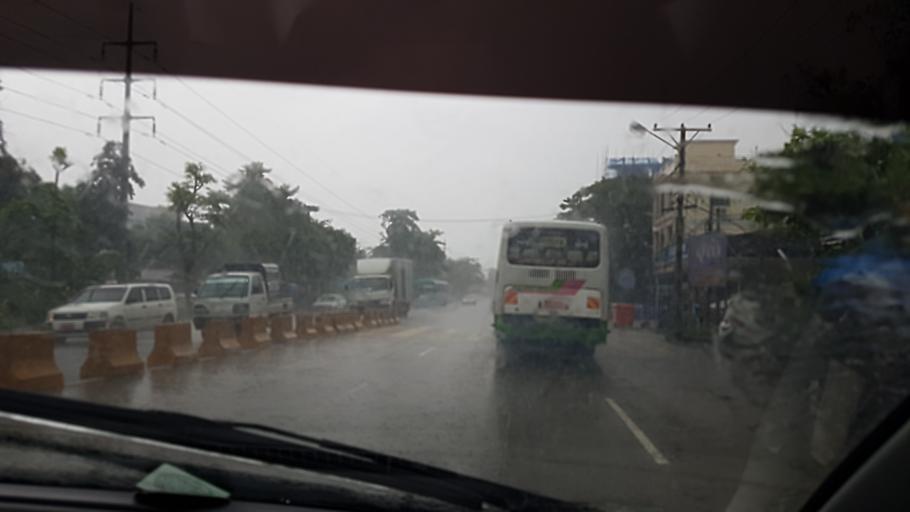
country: MM
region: Yangon
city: Yangon
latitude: 16.7776
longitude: 96.1955
